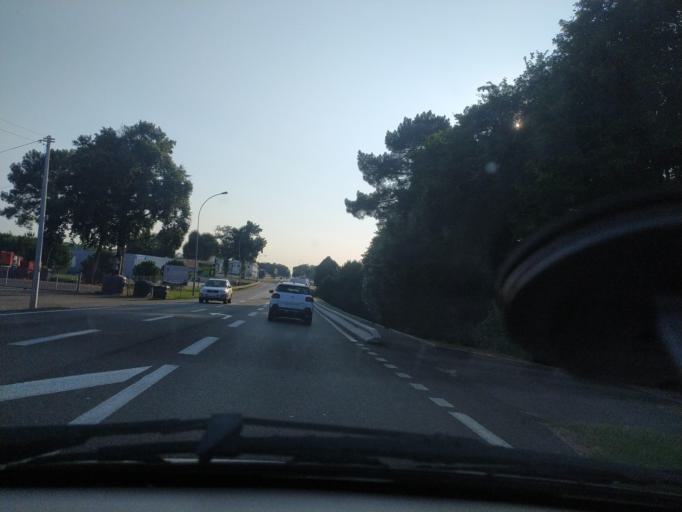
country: FR
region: Aquitaine
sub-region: Departement des Landes
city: Saint-Geours-de-Maremne
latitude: 43.6849
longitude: -1.2368
